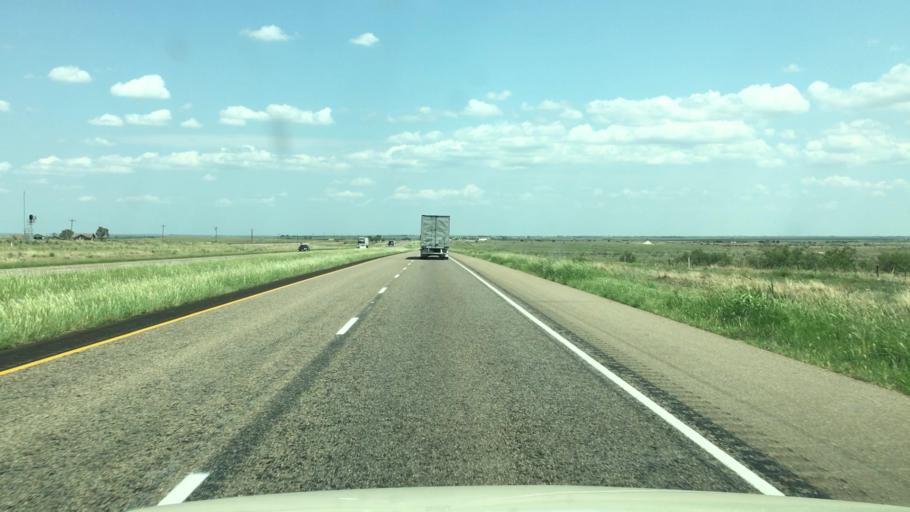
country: US
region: Texas
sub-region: Armstrong County
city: Claude
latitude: 35.0326
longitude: -101.1475
